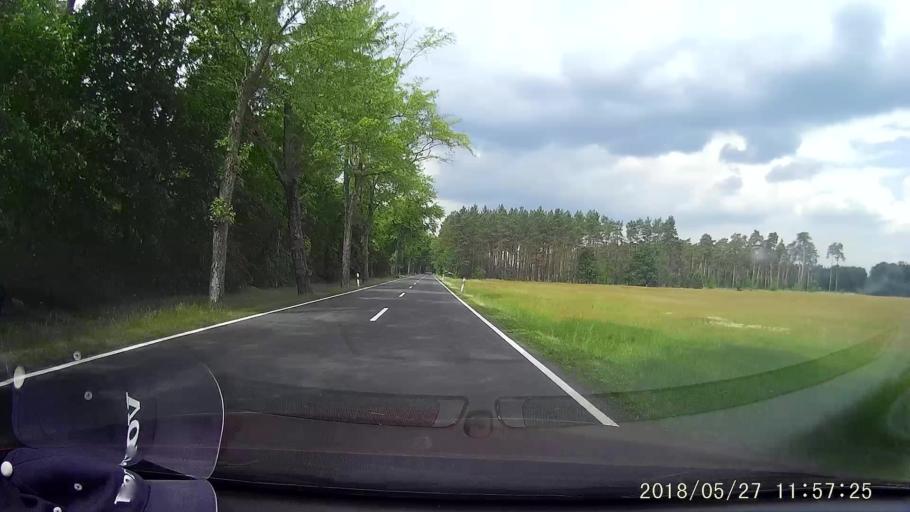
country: DE
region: Saxony
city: Mucka
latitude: 51.3049
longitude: 14.7240
